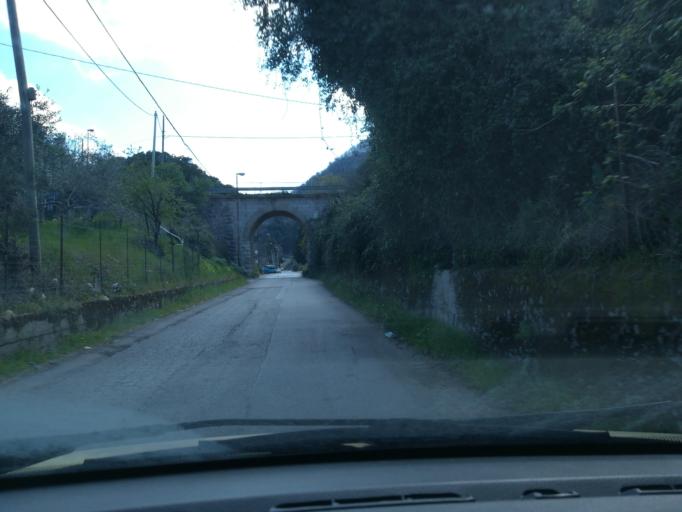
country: IT
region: Sicily
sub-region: Palermo
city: Altofonte
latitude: 38.0414
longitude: 13.2884
